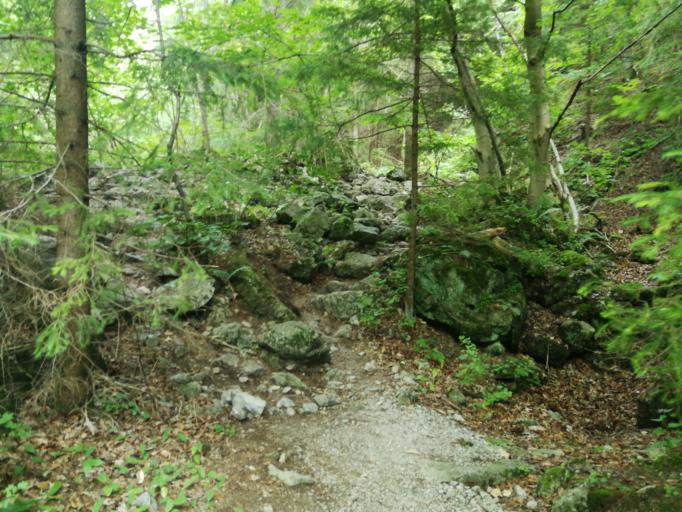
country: SK
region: Zilinsky
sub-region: Okres Liptovsky Mikulas
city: Liptovsky Mikulas
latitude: 49.1774
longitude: 19.4890
